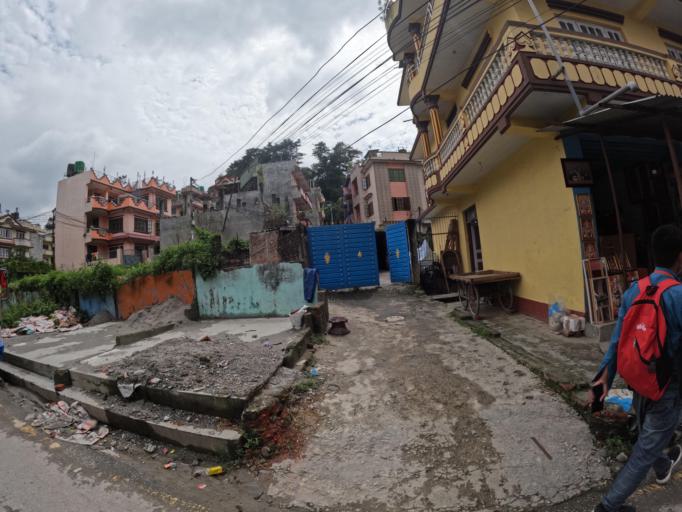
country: NP
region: Central Region
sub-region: Bagmati Zone
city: Kathmandu
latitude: 27.7492
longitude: 85.3178
